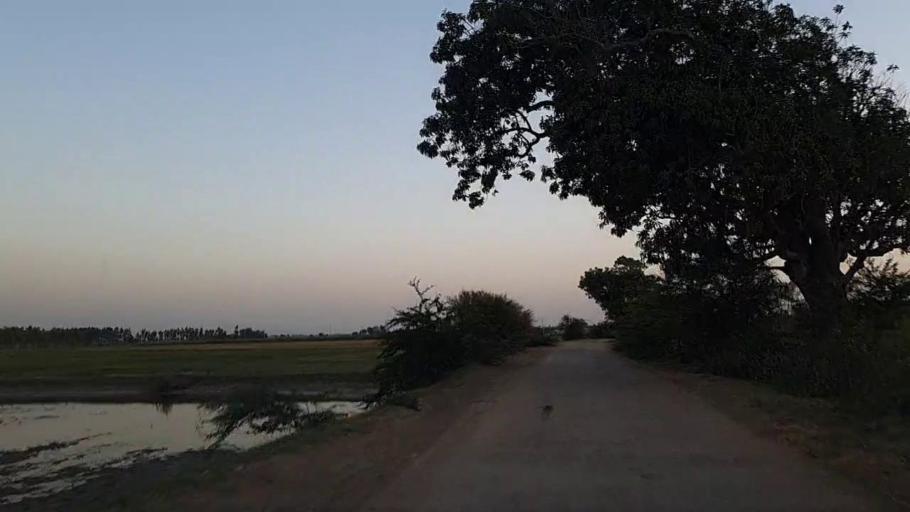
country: PK
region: Sindh
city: Mirpur Batoro
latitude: 24.6159
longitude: 68.1846
